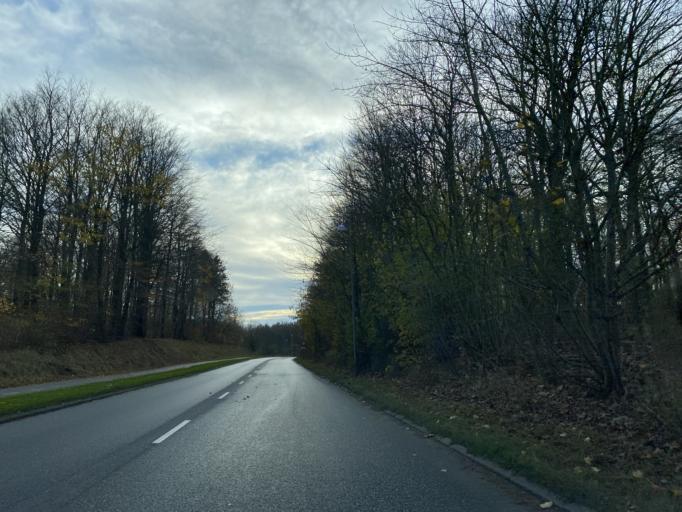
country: DK
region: South Denmark
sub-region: Aabenraa Kommune
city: Aabenraa
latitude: 55.0642
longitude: 9.3704
